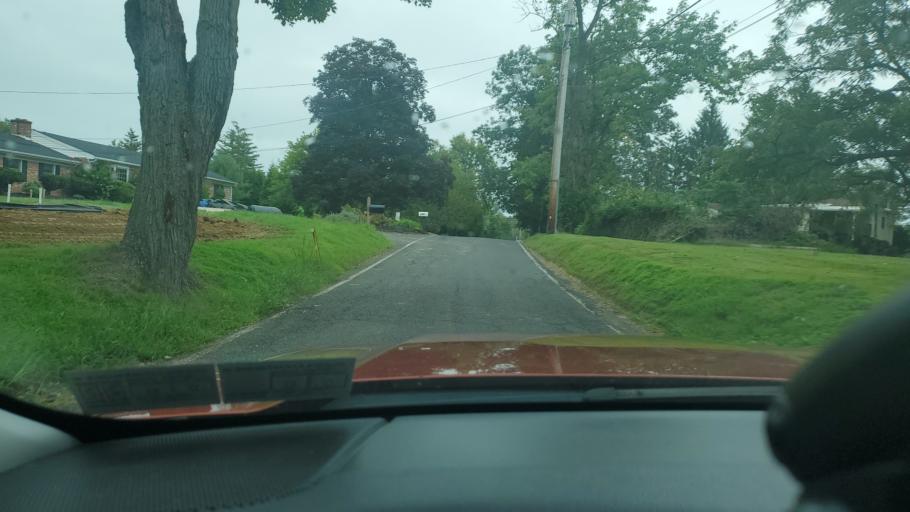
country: US
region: Pennsylvania
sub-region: Montgomery County
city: Woxall
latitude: 40.3055
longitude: -75.4815
